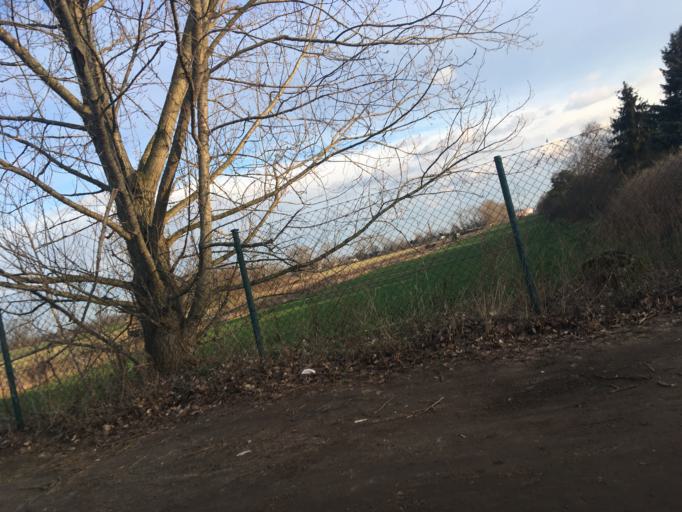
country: DE
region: Berlin
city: Buchholz
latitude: 52.6211
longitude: 13.4206
